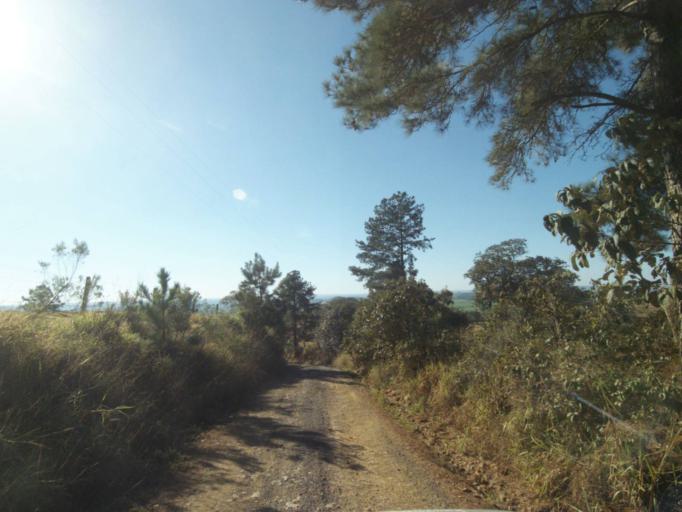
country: BR
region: Parana
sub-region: Tibagi
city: Tibagi
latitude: -24.5399
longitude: -50.4683
